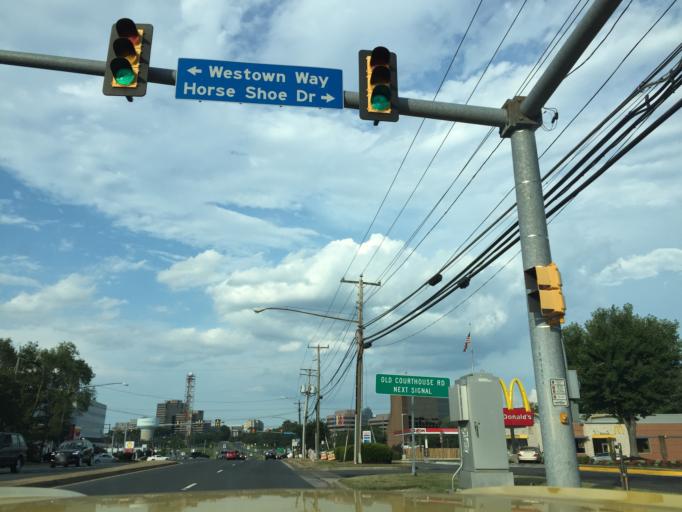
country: US
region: Virginia
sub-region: Fairfax County
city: Tysons Corner
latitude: 38.9158
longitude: -77.2390
